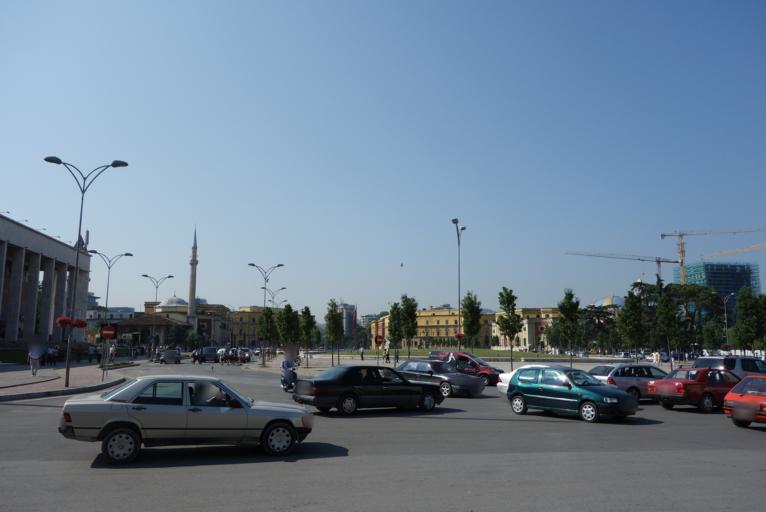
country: AL
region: Tirane
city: Tirana
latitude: 41.3293
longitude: 19.8185
